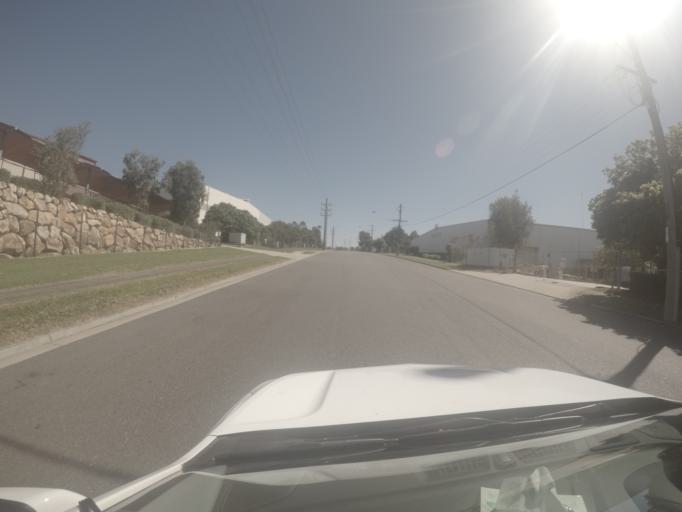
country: AU
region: Queensland
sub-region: Brisbane
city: Richlands
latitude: -27.5803
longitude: 152.9504
